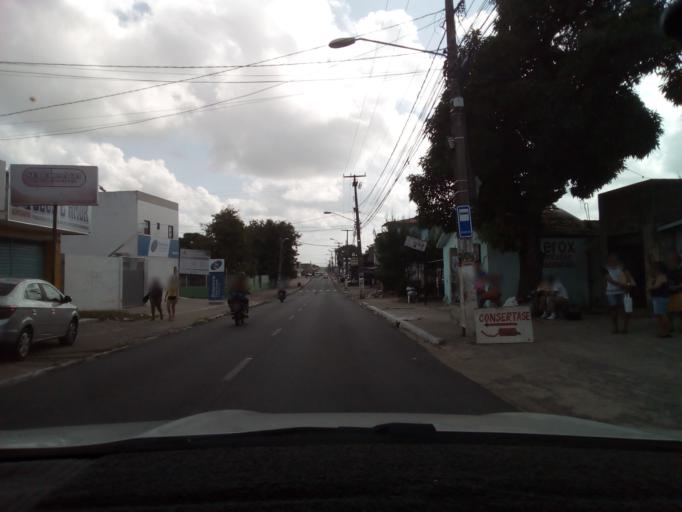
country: BR
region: Paraiba
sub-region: Bayeux
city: Bayeux
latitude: -7.1234
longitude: -34.9188
